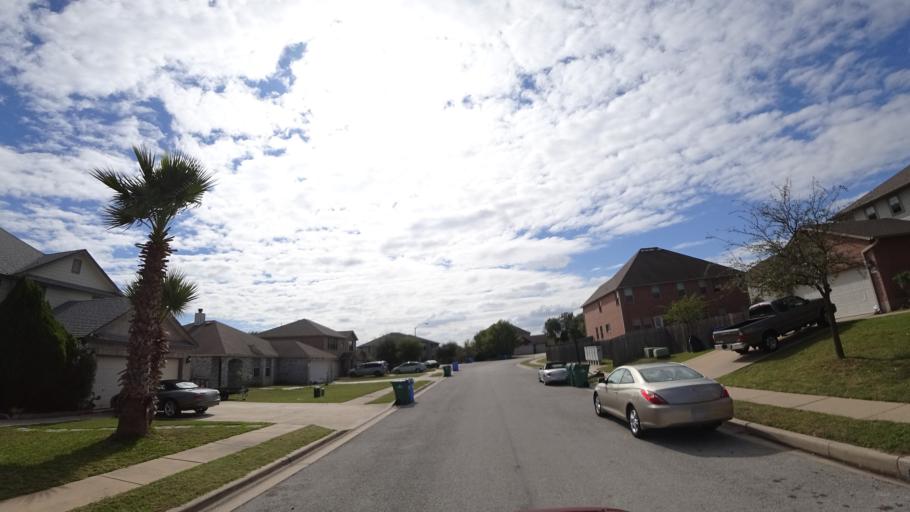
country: US
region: Texas
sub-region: Travis County
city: Pflugerville
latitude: 30.4461
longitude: -97.6269
